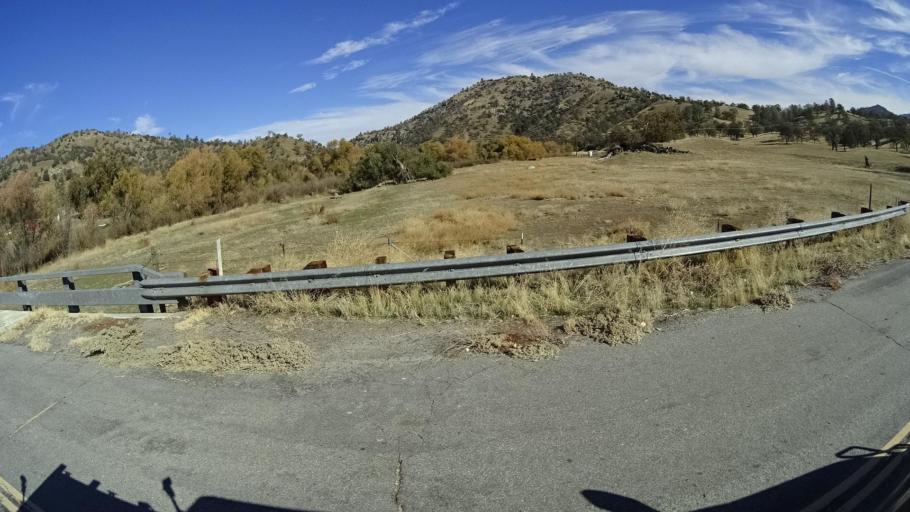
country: US
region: California
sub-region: Kern County
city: Alta Sierra
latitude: 35.6262
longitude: -118.7492
